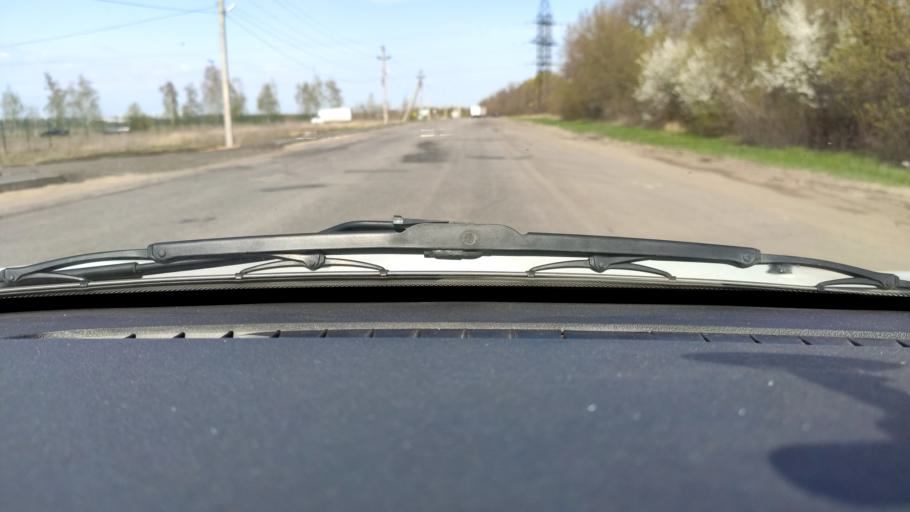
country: RU
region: Voronezj
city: Novaya Usman'
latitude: 51.6284
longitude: 39.3340
